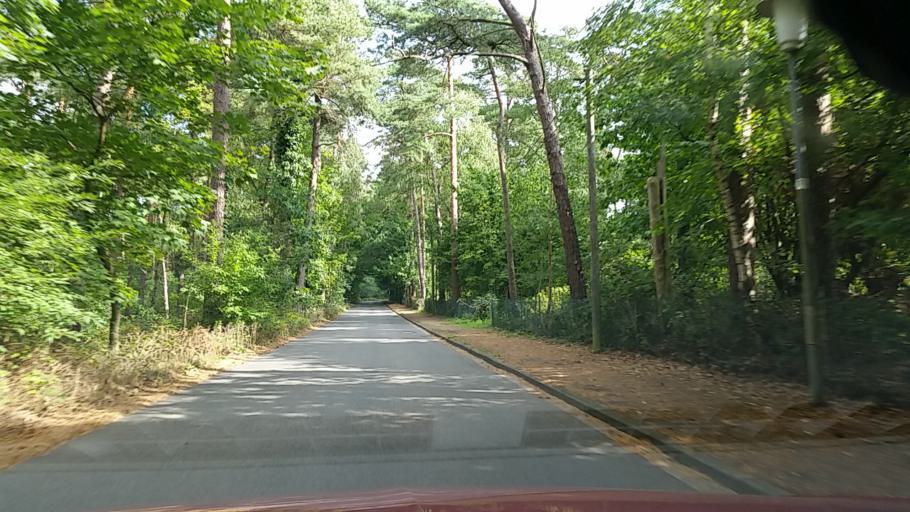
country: DE
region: Schleswig-Holstein
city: Wedel
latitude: 53.5911
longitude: 9.7447
